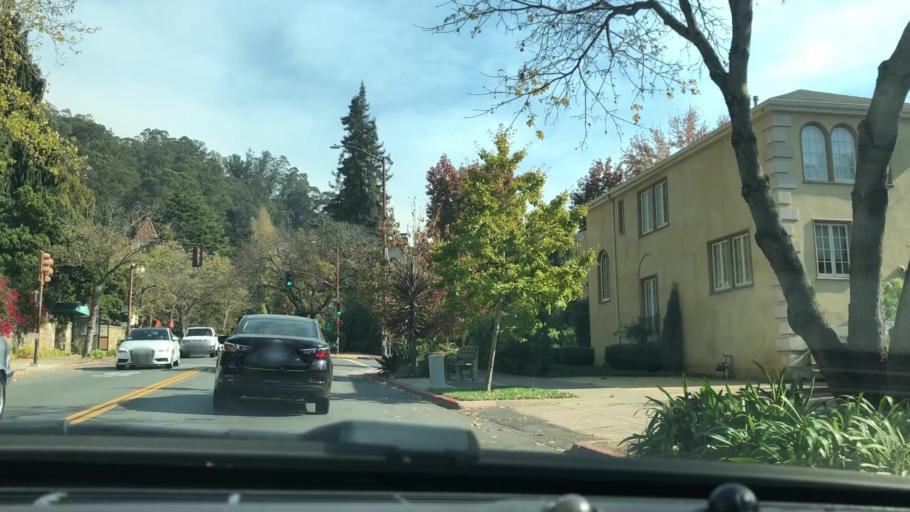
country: US
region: California
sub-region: Alameda County
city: Berkeley
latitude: 37.8624
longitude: -122.2477
